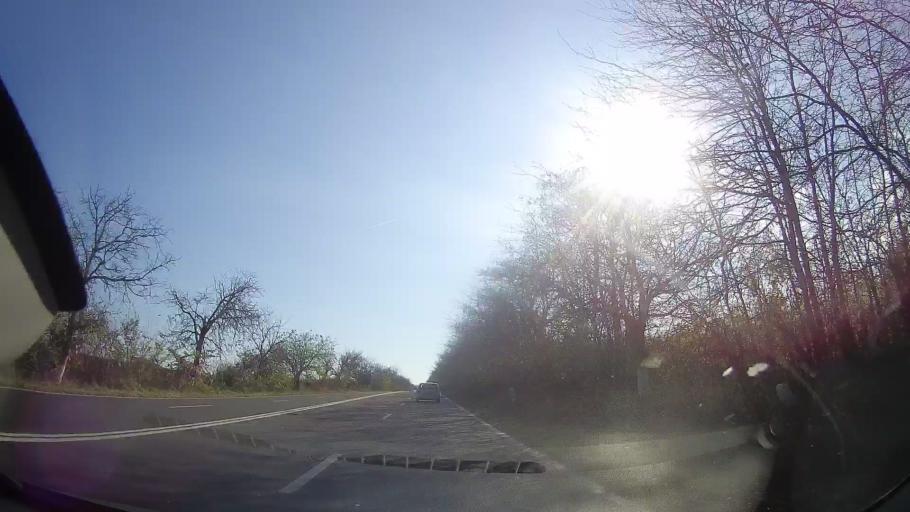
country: RO
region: Constanta
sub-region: Comuna Douazeci si Trei August
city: Douazeci si Trei August
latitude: 43.8937
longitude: 28.5719
